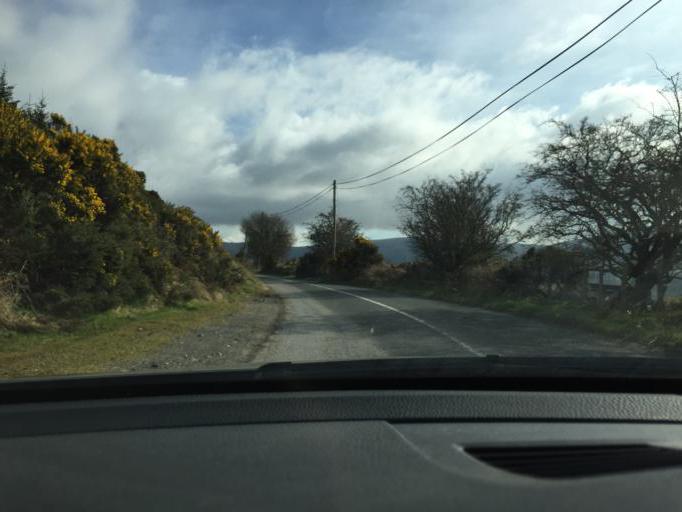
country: IE
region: Leinster
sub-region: Wicklow
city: Valleymount
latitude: 53.0725
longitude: -6.5324
